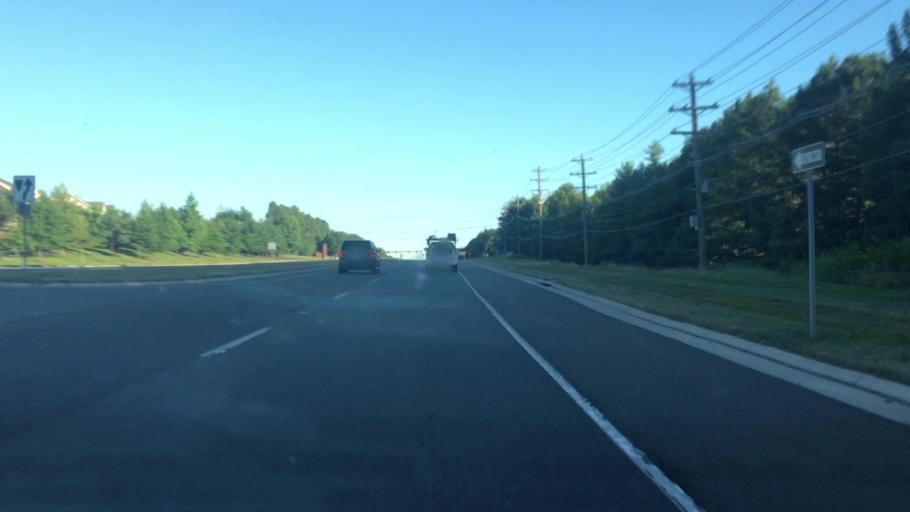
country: US
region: Virginia
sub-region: Prince William County
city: Haymarket
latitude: 38.8476
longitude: -77.6372
